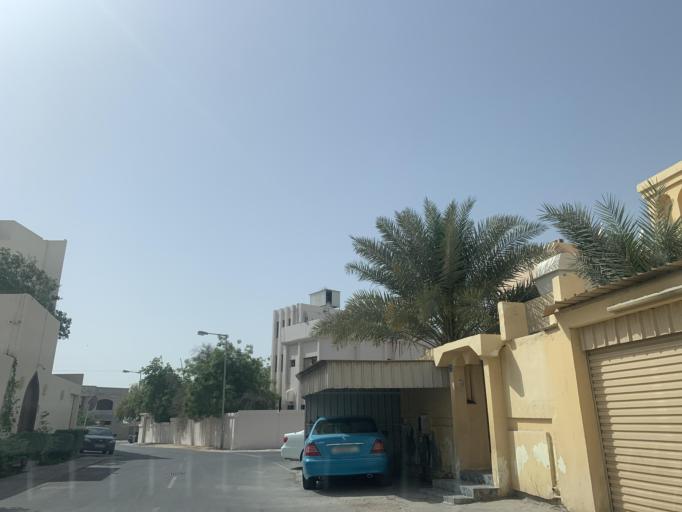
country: BH
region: Northern
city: Ar Rifa'
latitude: 26.1448
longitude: 50.5676
